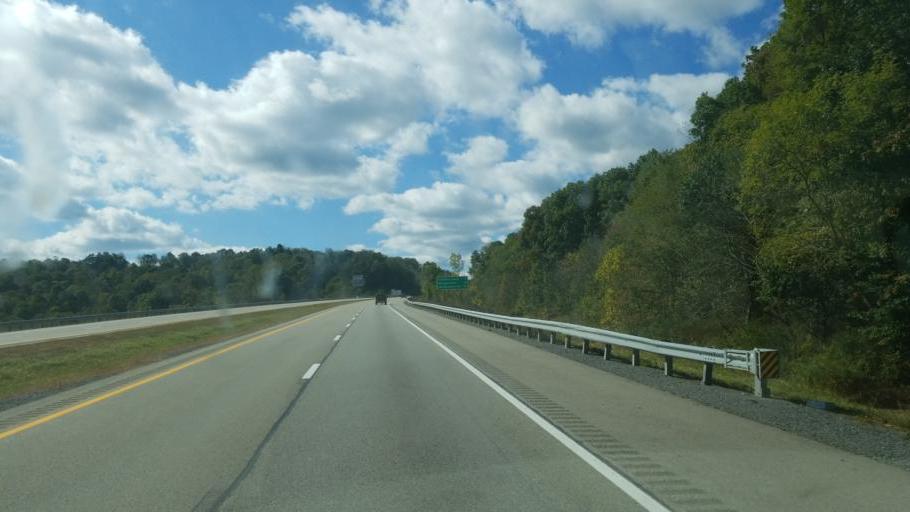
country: US
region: West Virginia
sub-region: Preston County
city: Kingwood
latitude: 39.6566
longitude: -79.6522
